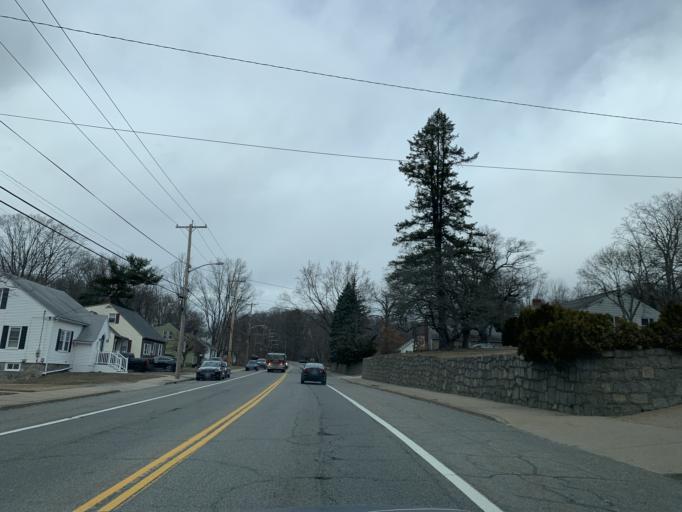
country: US
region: Rhode Island
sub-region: Providence County
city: Cumberland Hill
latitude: 42.0102
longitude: -71.4777
